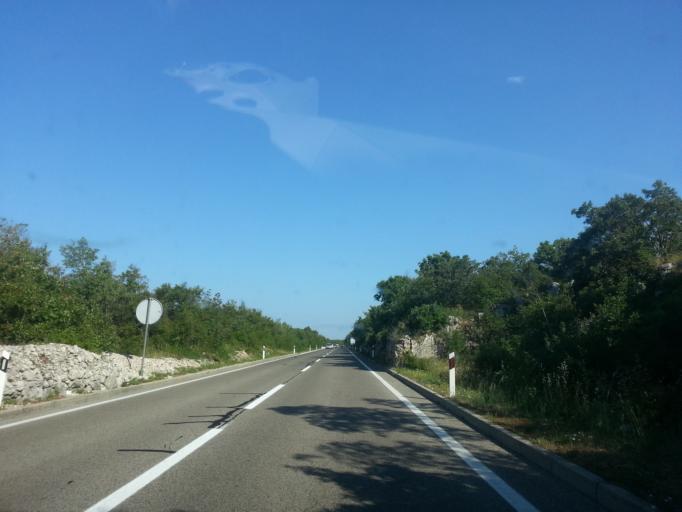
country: HR
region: Primorsko-Goranska
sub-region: Grad Crikvenica
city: Jadranovo
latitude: 45.2461
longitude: 14.6064
